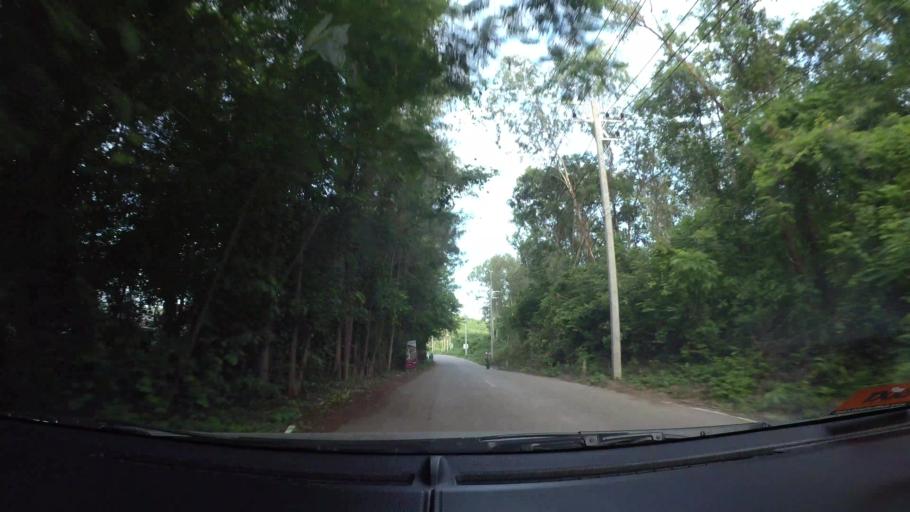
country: TH
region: Chon Buri
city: Sattahip
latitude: 12.7531
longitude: 100.9507
